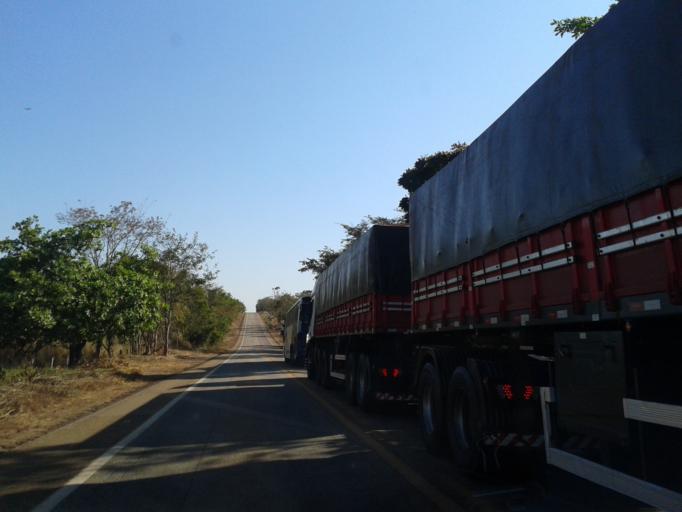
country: BR
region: Goias
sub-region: Mozarlandia
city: Mozarlandia
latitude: -14.7373
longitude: -50.5441
